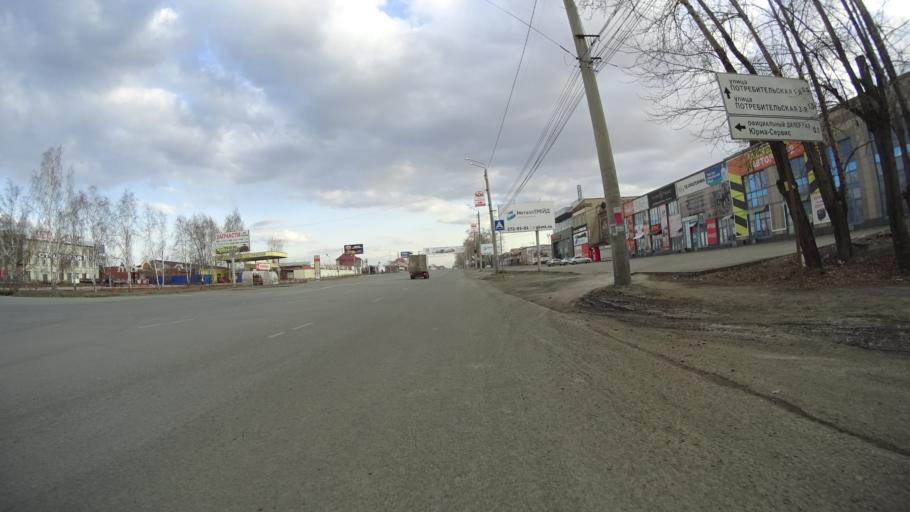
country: RU
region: Chelyabinsk
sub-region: Gorod Chelyabinsk
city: Chelyabinsk
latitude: 55.1123
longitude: 61.3866
